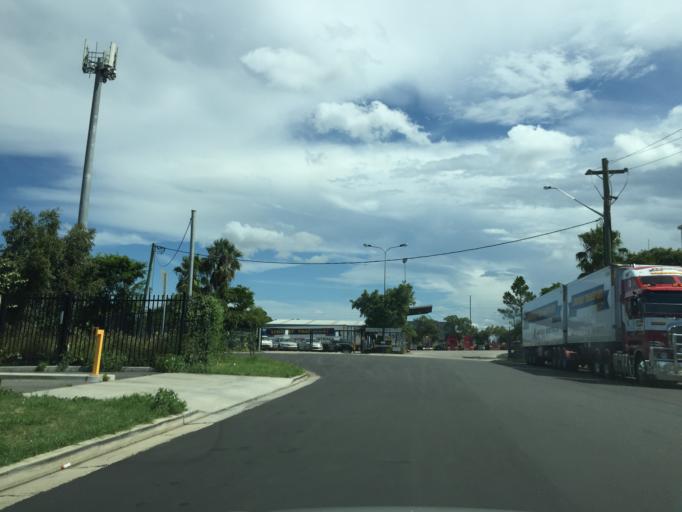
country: AU
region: New South Wales
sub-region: Blacktown
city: Doonside
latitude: -33.7924
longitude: 150.8838
